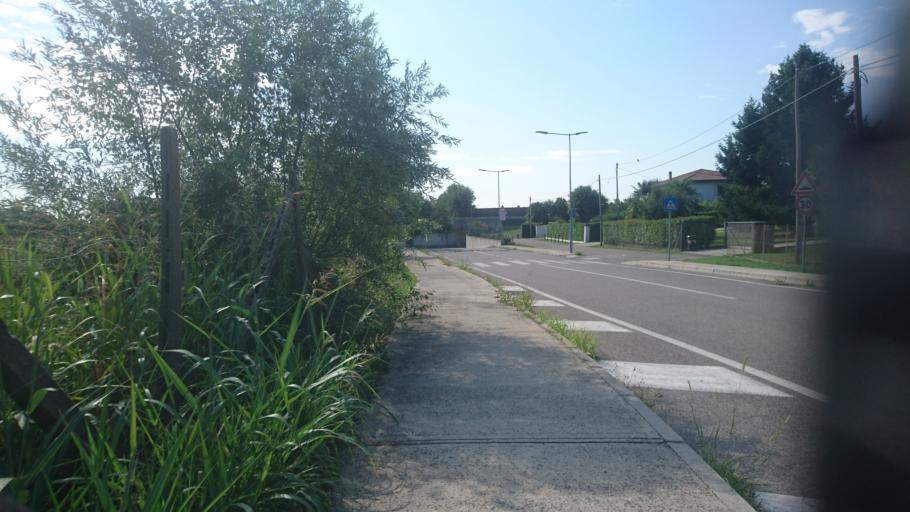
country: IT
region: Veneto
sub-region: Provincia di Padova
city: Tencarola
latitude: 45.3841
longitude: 11.8120
